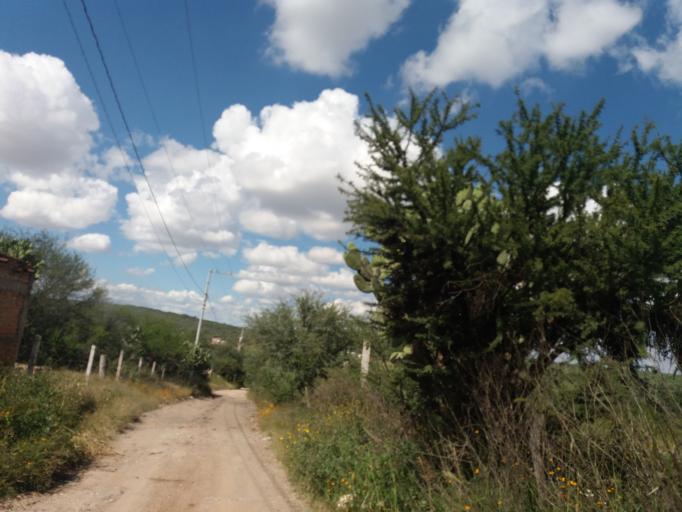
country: MX
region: Aguascalientes
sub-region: Aguascalientes
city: San Sebastian [Fraccionamiento]
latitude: 21.8055
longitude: -102.2420
